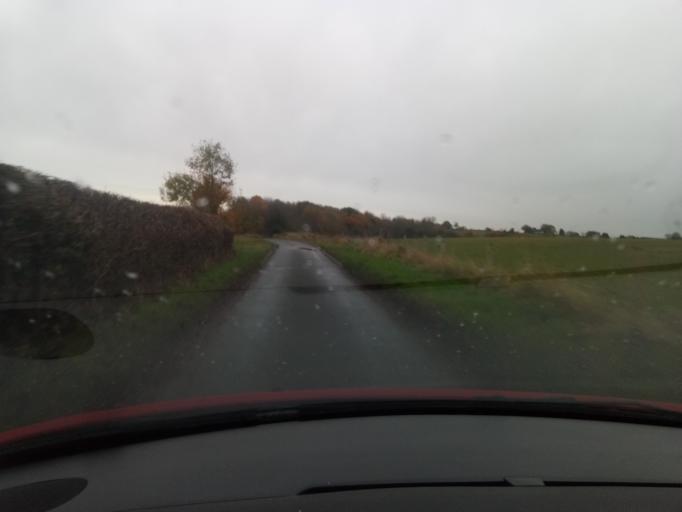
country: GB
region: England
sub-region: Derbyshire
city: Borrowash
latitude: 52.8683
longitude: -1.4101
